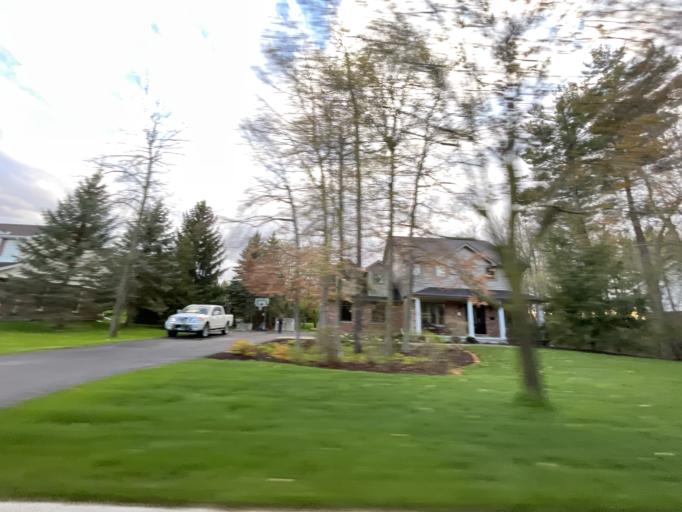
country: CA
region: Ontario
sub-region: Wellington County
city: Guelph
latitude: 43.5860
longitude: -80.2819
